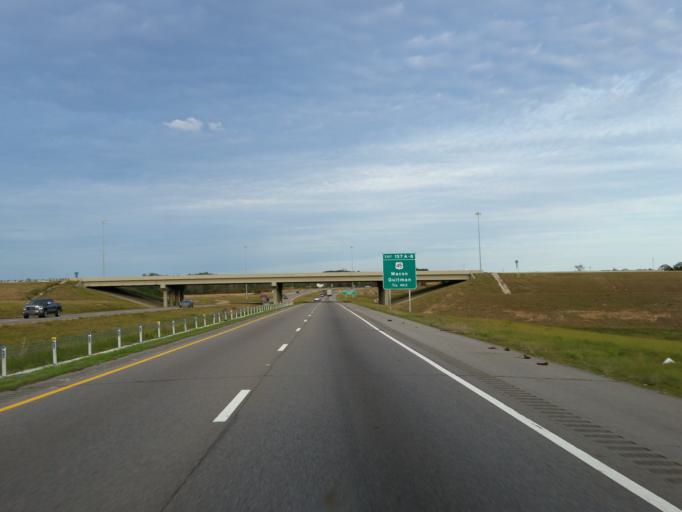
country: US
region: Mississippi
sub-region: Lauderdale County
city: Marion
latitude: 32.3776
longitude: -88.6565
